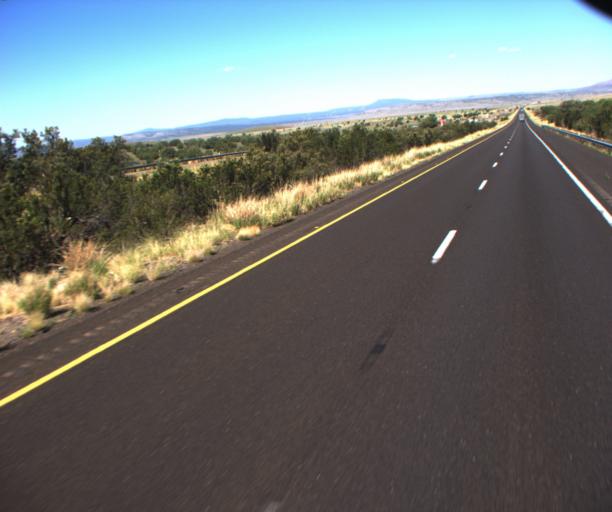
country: US
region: Arizona
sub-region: Yavapai County
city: Paulden
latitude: 35.2819
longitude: -112.7896
